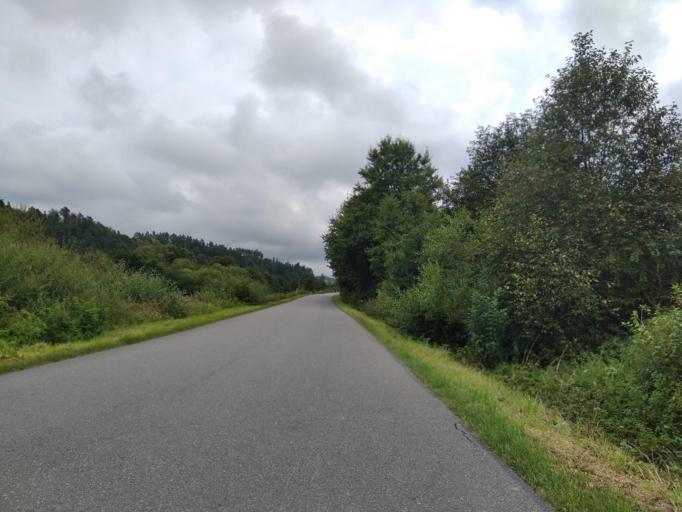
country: PL
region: Subcarpathian Voivodeship
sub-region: Powiat brzozowski
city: Nozdrzec
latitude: 49.7407
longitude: 22.2440
